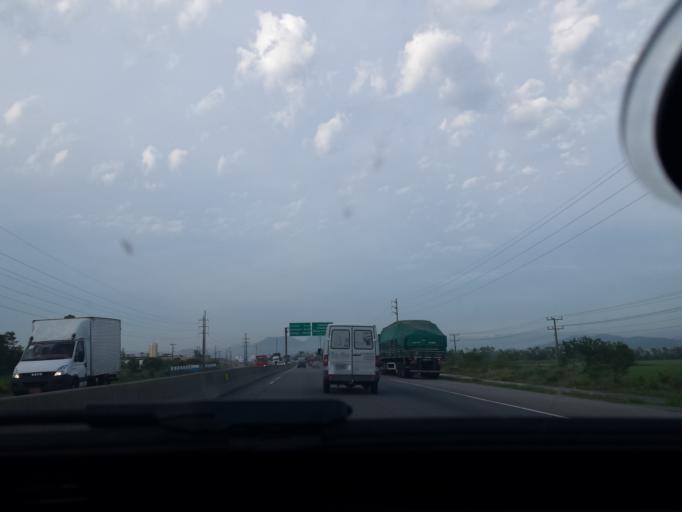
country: BR
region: Santa Catarina
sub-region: Tubarao
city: Tubarao
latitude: -28.4572
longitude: -48.9845
